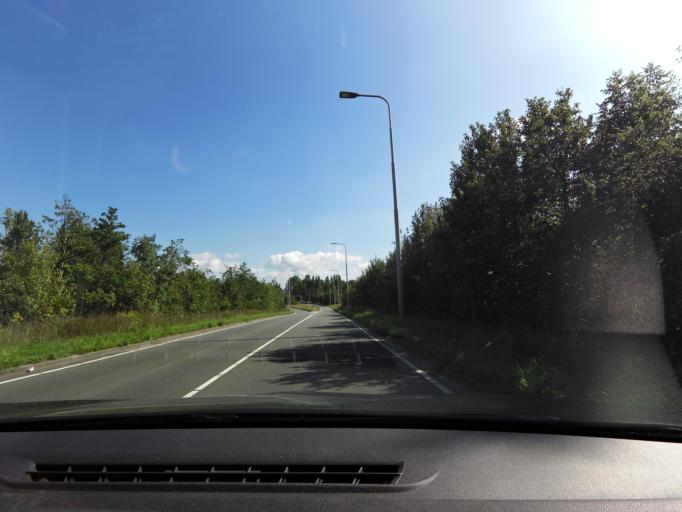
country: NL
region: North Holland
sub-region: Gemeente Amstelveen
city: Amstelveen
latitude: 52.2876
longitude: 4.8308
